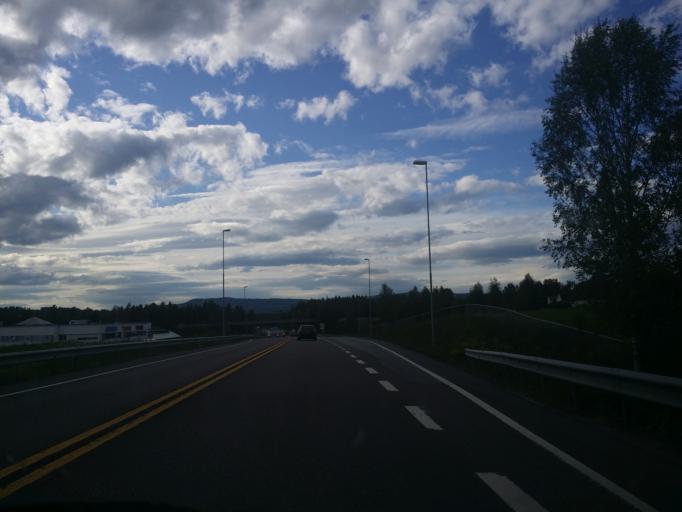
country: NO
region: Hedmark
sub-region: Hamar
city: Hamar
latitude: 60.7978
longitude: 11.1198
